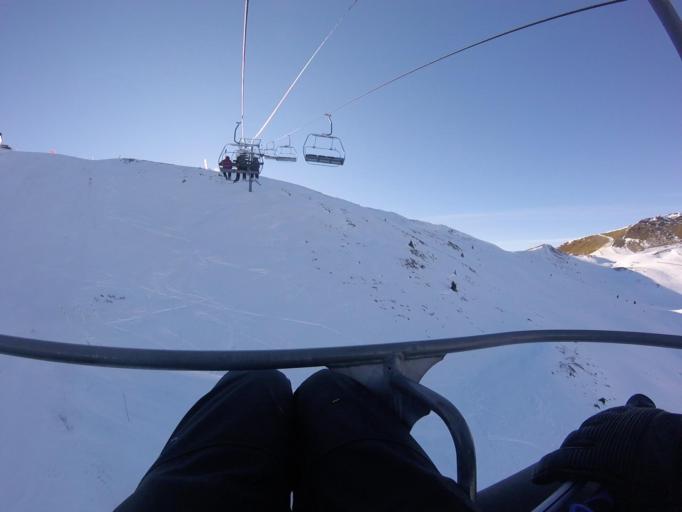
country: AD
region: Canillo
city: El Tarter
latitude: 42.5476
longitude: 1.6587
